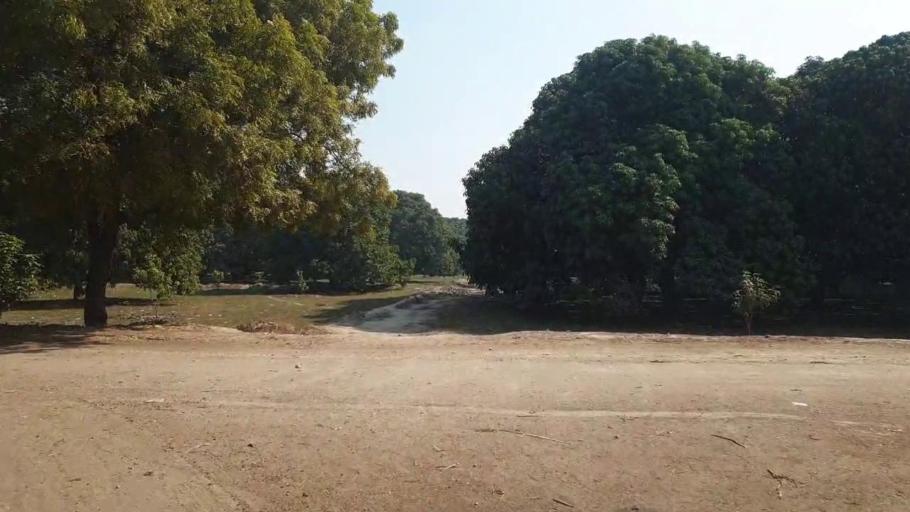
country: PK
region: Sindh
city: Tando Jam
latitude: 25.3468
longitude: 68.6306
